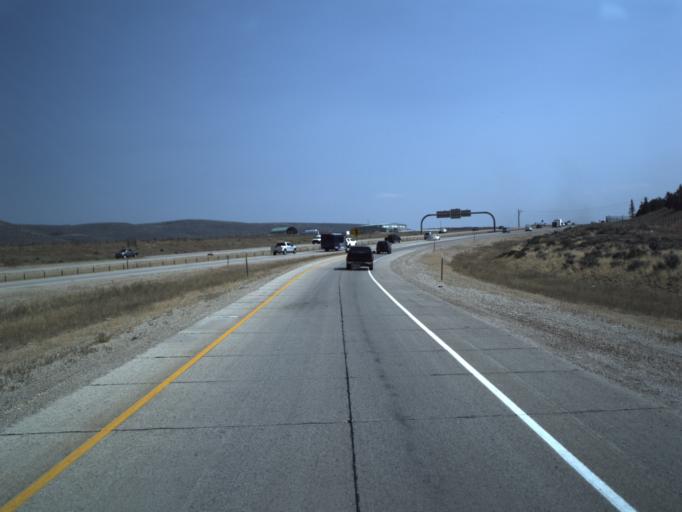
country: US
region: Utah
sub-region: Summit County
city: Snyderville
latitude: 40.7160
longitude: -111.4866
